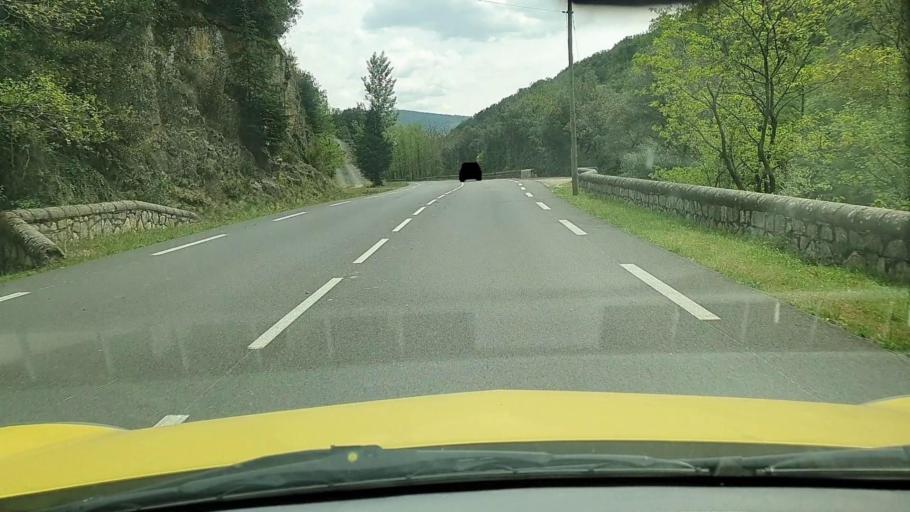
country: FR
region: Languedoc-Roussillon
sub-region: Departement du Gard
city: Valleraugue
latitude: 44.0649
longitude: 3.6808
